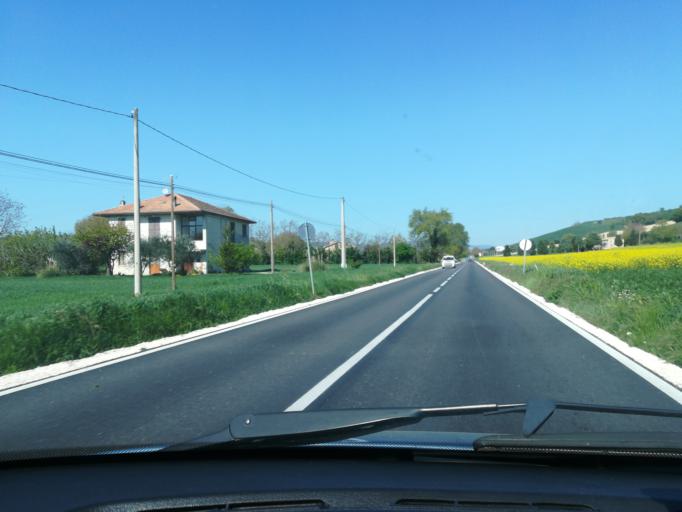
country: IT
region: The Marches
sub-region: Provincia di Macerata
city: Villa Potenza
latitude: 43.3263
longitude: 13.4032
